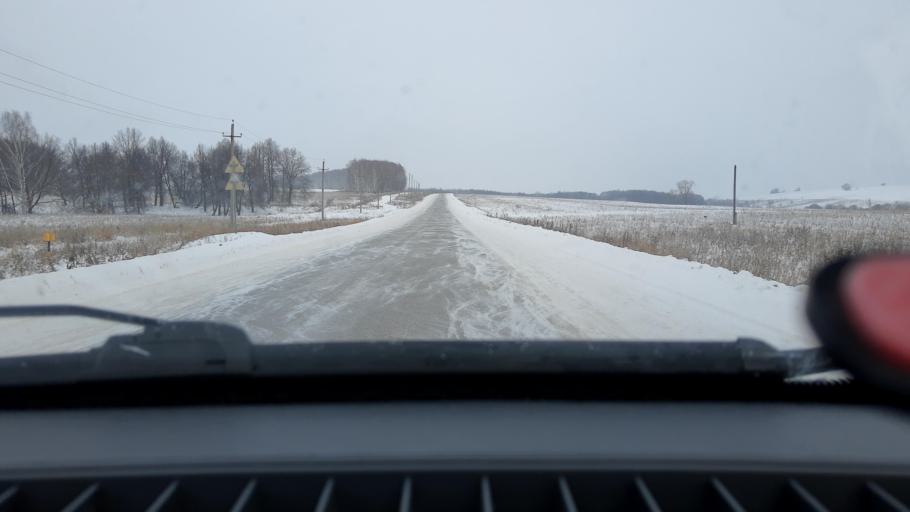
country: RU
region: Bashkortostan
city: Iglino
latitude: 54.6453
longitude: 56.4249
